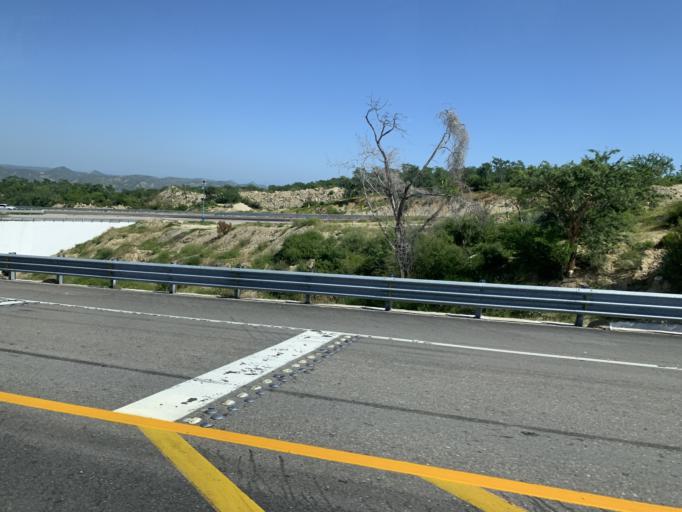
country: MX
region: Baja California Sur
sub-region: Los Cabos
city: San Jose del Cabo
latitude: 23.0734
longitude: -109.7479
